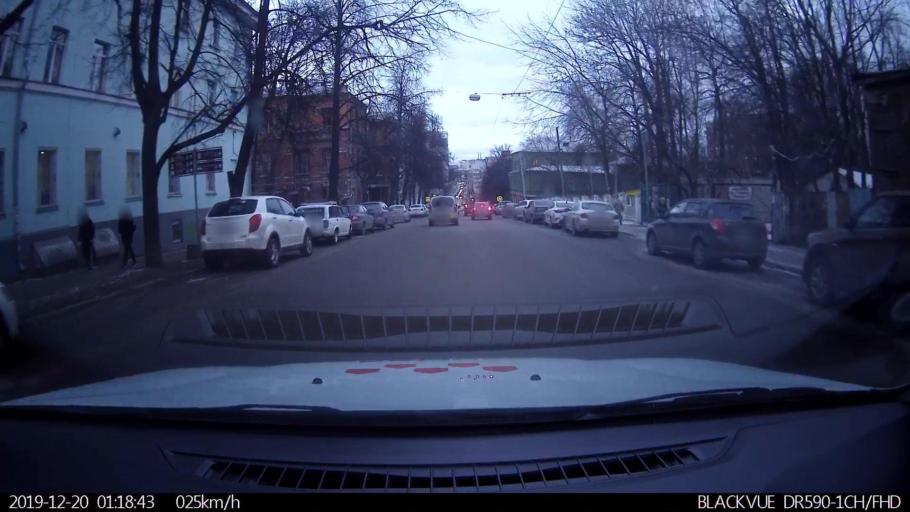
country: RU
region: Nizjnij Novgorod
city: Nizhniy Novgorod
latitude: 56.3235
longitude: 44.0195
